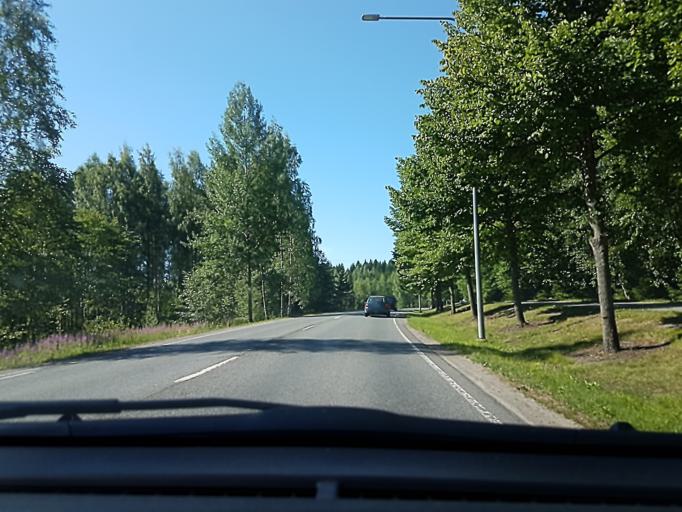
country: FI
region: Uusimaa
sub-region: Helsinki
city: Vantaa
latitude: 60.3388
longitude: 25.0694
